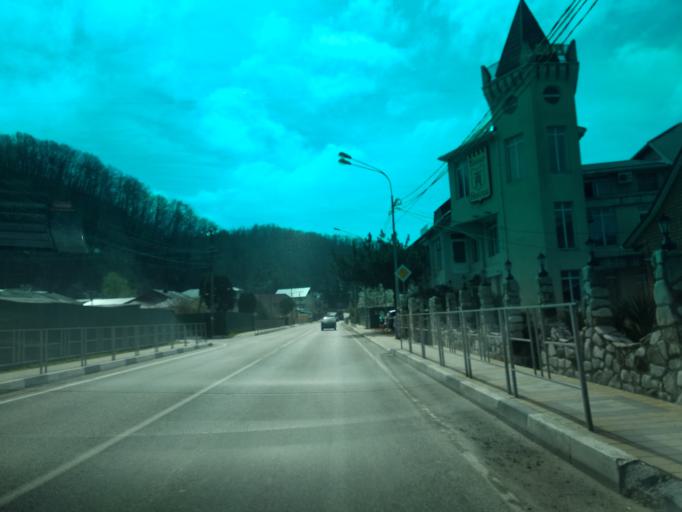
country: RU
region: Krasnodarskiy
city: Shepsi
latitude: 44.0398
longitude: 39.1507
